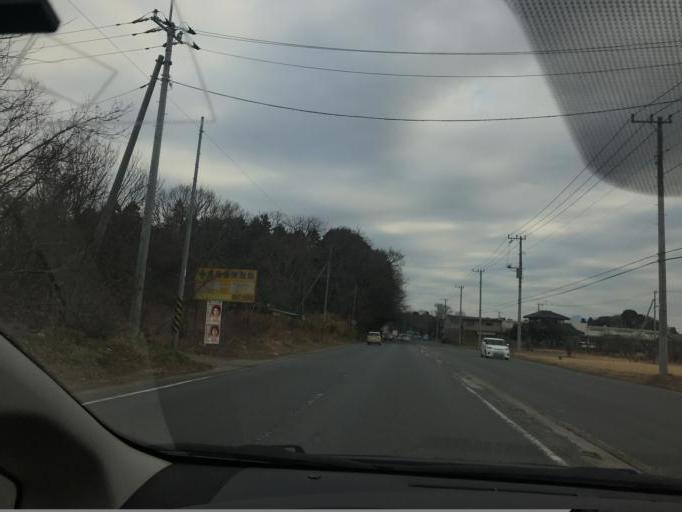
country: JP
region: Ibaraki
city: Ishige
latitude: 36.0826
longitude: 140.0389
